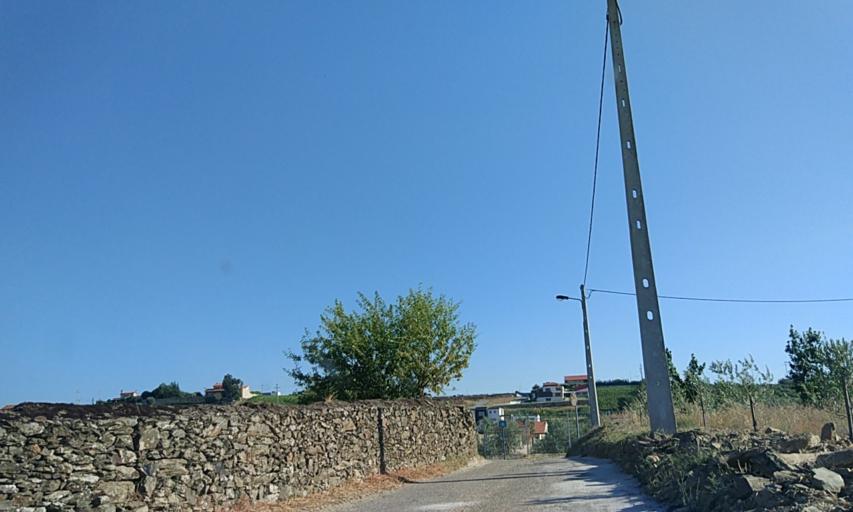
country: PT
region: Viseu
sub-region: Sao Joao da Pesqueira
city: Sao Joao da Pesqueira
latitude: 41.1533
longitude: -7.4201
